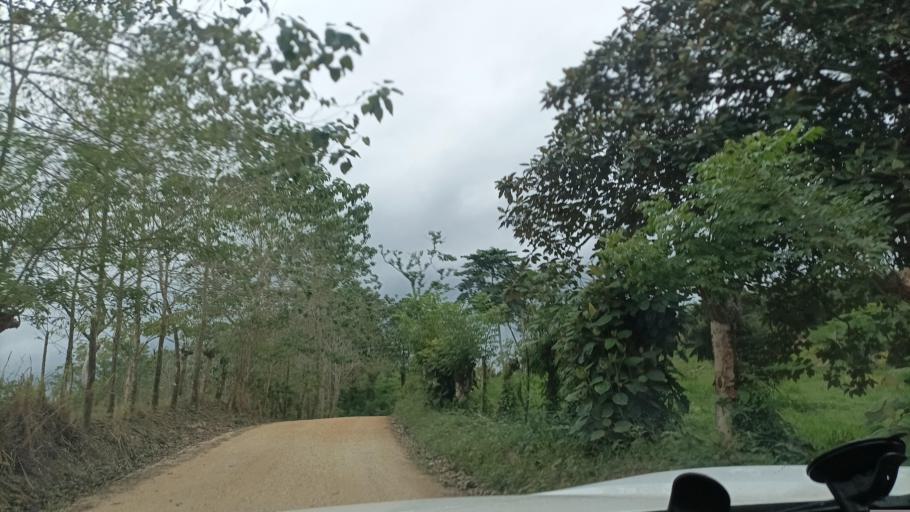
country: MX
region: Veracruz
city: Hidalgotitlan
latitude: 17.6289
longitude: -94.5116
